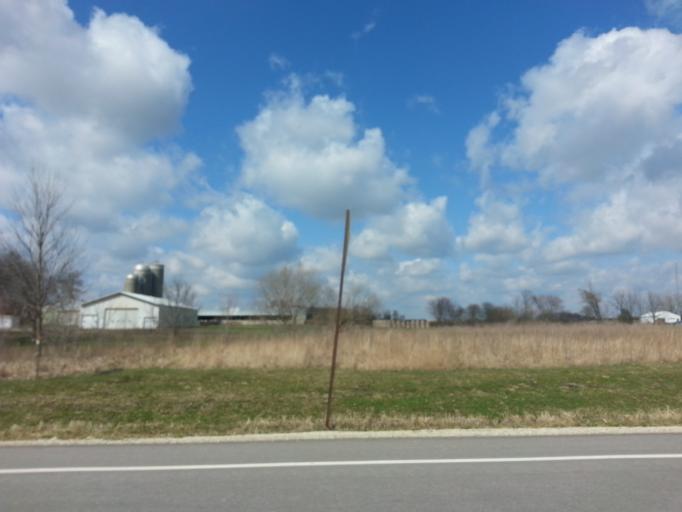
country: US
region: Minnesota
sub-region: Dodge County
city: Dodge Center
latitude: 44.0805
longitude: -92.8208
